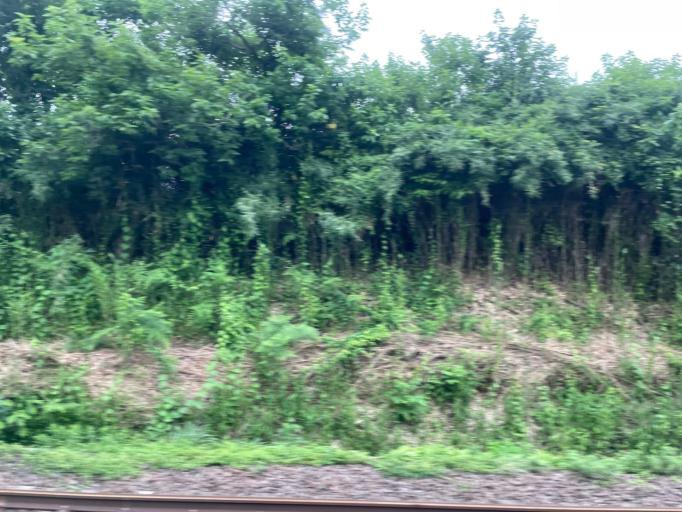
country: JP
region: Fukushima
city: Nihommatsu
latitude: 37.6435
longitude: 140.4827
